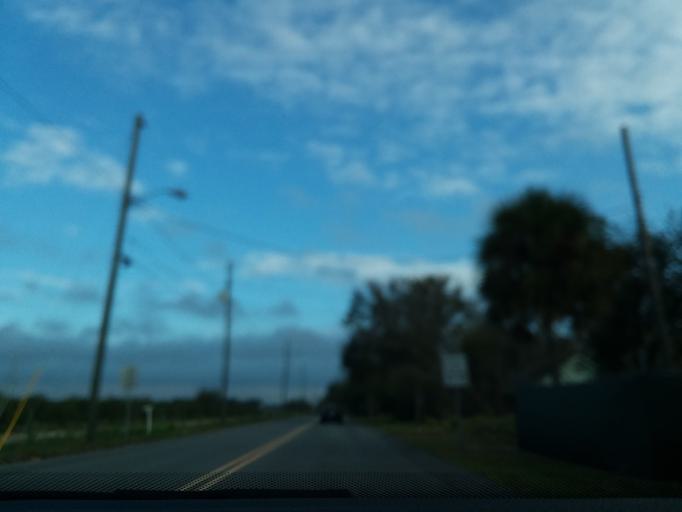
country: US
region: Florida
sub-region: Polk County
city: Haines City
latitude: 28.1167
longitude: -81.6526
